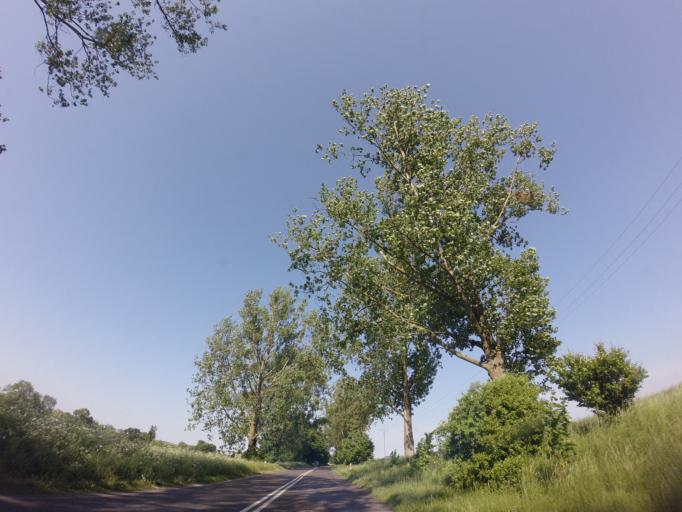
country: PL
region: West Pomeranian Voivodeship
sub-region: Powiat stargardzki
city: Kobylanka
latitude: 53.3110
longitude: 14.8370
